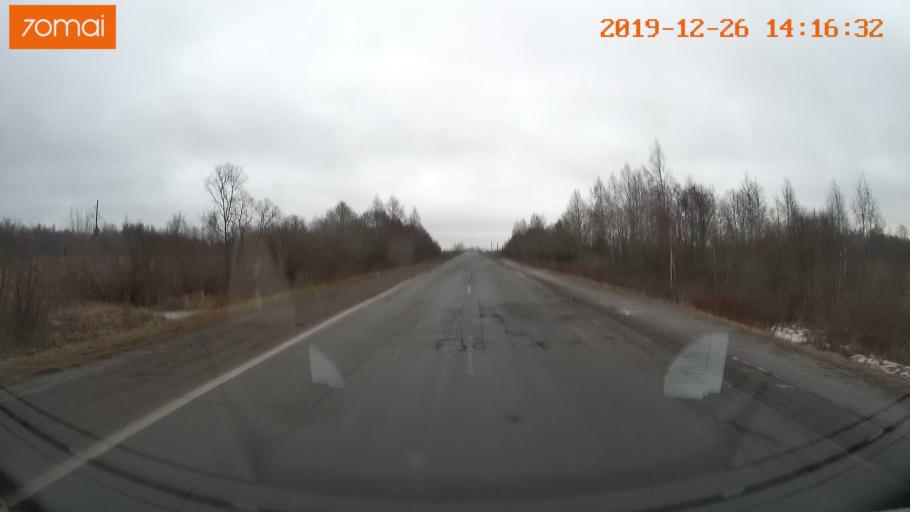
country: RU
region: Jaroslavl
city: Poshekhon'ye
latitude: 58.5170
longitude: 39.0645
